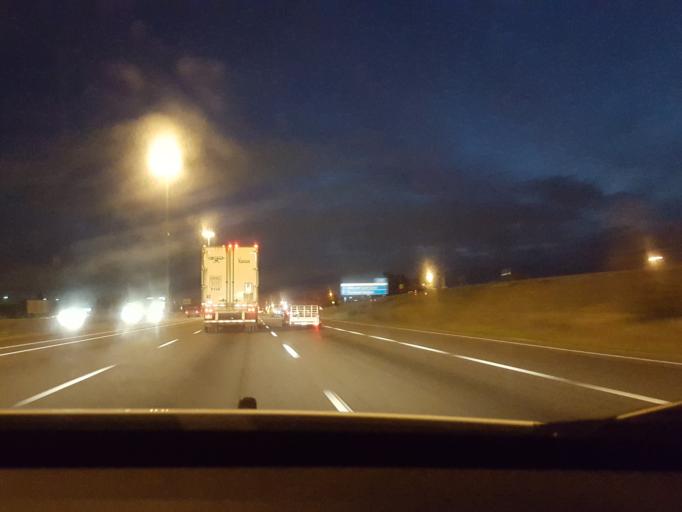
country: CA
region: Ontario
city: Burlington
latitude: 43.3808
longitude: -79.7725
